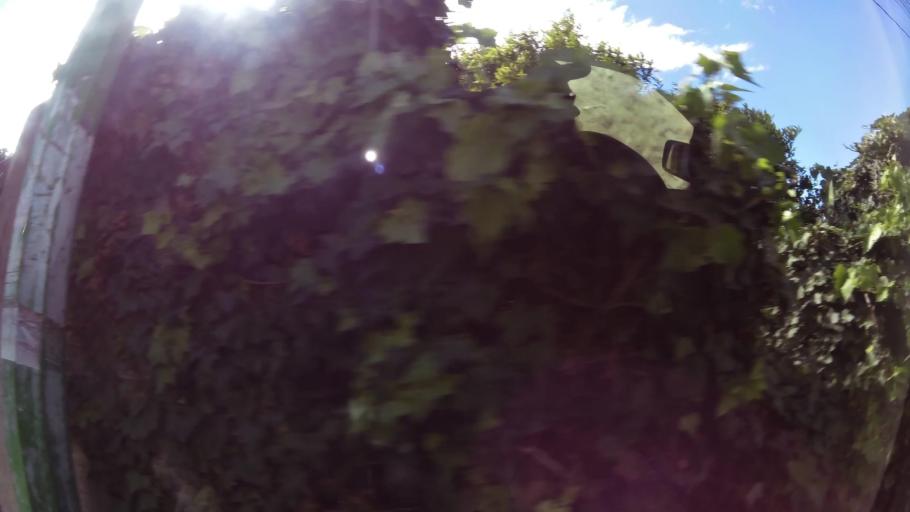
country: GT
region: Solola
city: Panajachel
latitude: 14.7363
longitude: -91.1511
